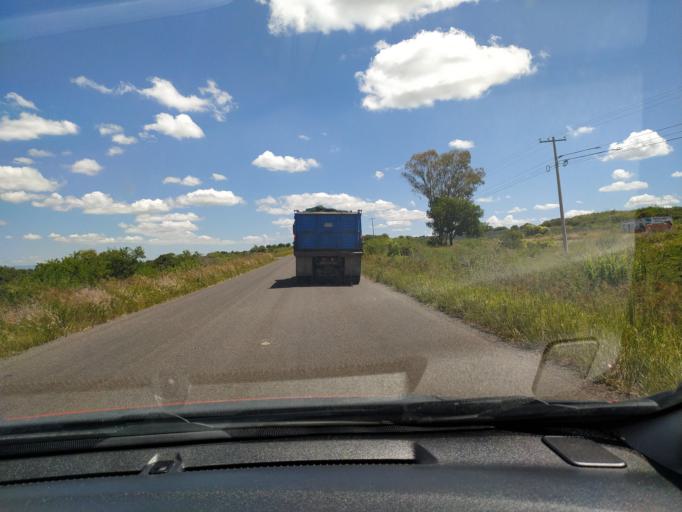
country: MX
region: Jalisco
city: San Diego de Alejandria
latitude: 21.0077
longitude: -102.0221
